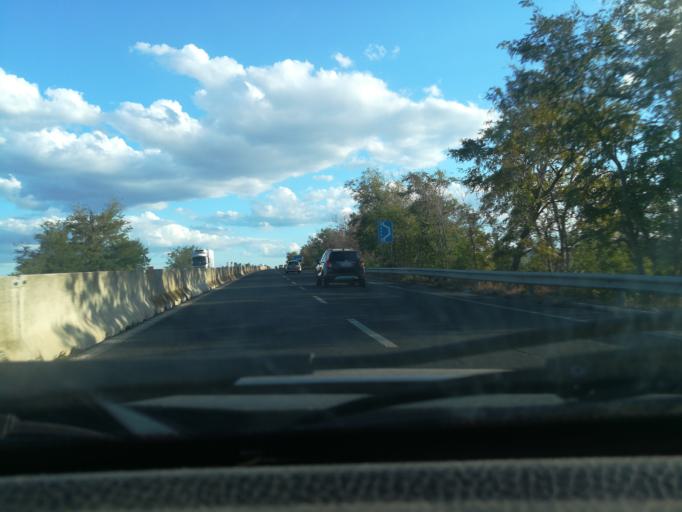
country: IT
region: Apulia
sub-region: Provincia di Bari
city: Mola di Bari
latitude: 41.0658
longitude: 17.0670
